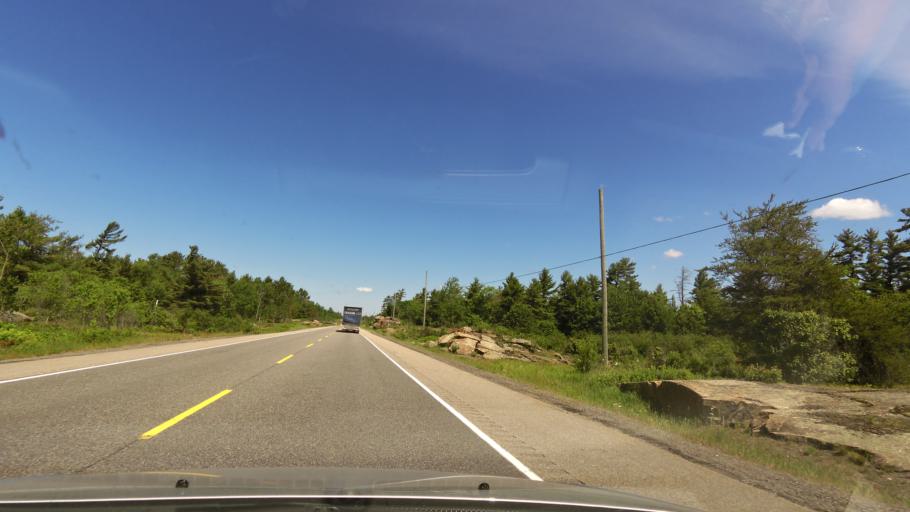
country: CA
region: Ontario
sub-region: Parry Sound District
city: Parry Sound
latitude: 45.7065
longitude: -80.4594
